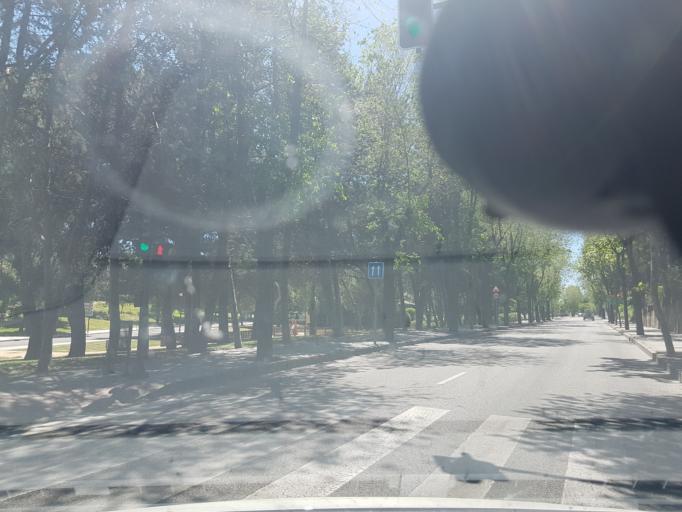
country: ES
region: Madrid
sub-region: Provincia de Madrid
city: Pozuelo de Alarcon
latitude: 40.4421
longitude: -3.8079
